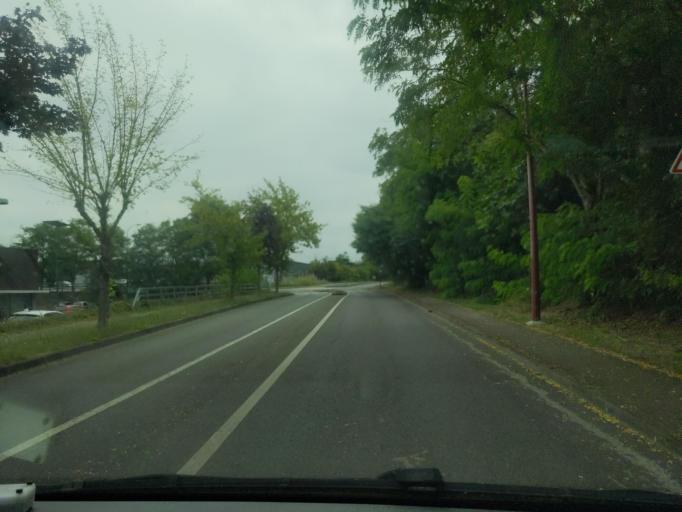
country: FR
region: Midi-Pyrenees
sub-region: Departement de la Haute-Garonne
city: Auzeville-Tolosane
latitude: 43.5358
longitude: 1.4768
